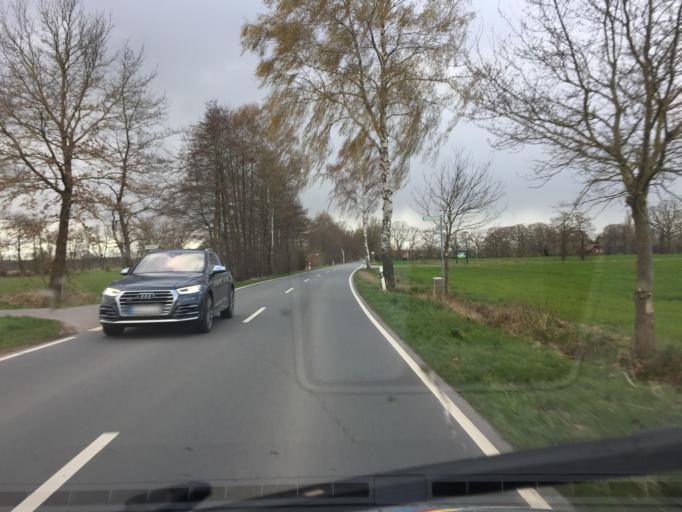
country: DE
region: Lower Saxony
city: Riede
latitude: 52.9458
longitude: 8.9241
